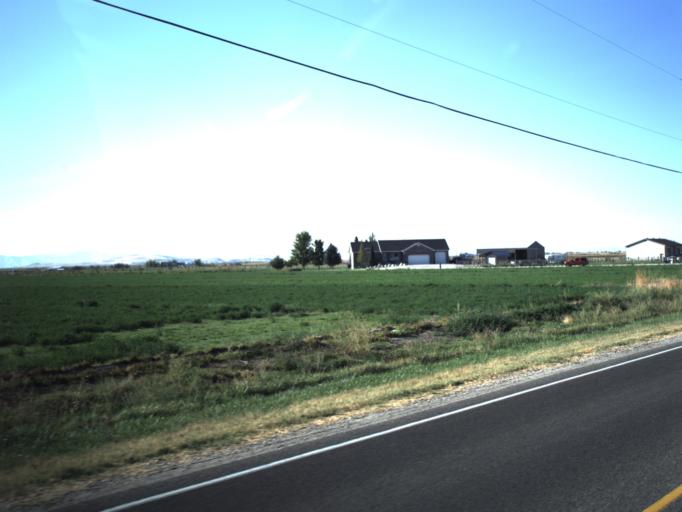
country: US
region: Utah
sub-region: Weber County
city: Hooper
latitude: 41.1811
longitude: -112.1226
